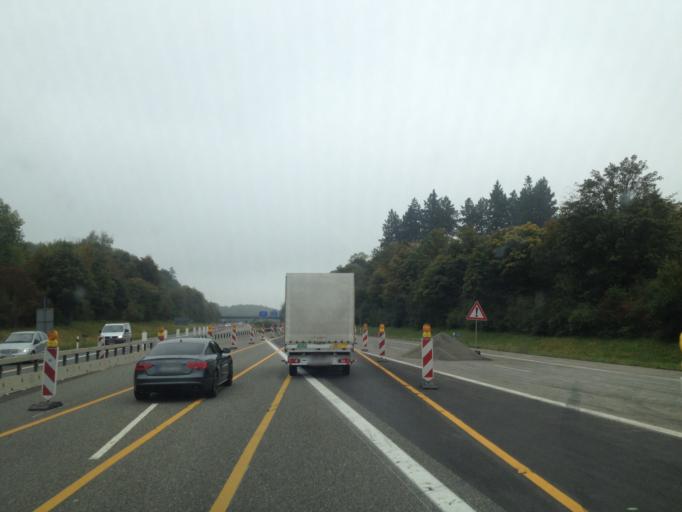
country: DE
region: Baden-Wuerttemberg
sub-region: Freiburg Region
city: Volkertshausen
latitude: 47.8196
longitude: 8.8427
